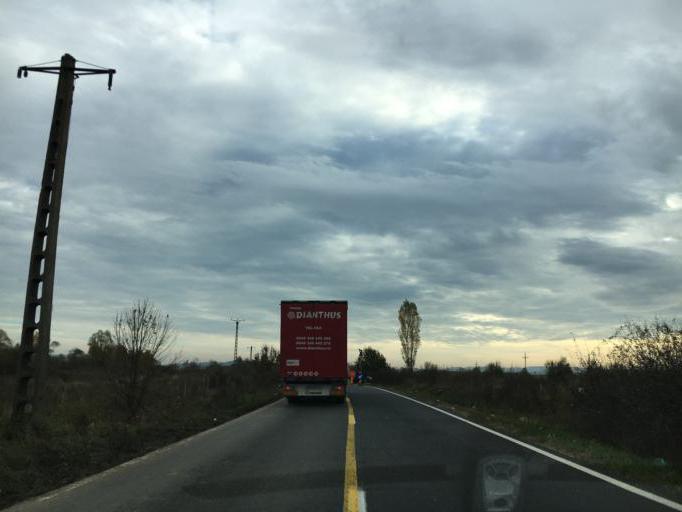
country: RO
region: Timis
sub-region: Comuna Margina
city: Margina
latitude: 45.8577
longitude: 22.2356
